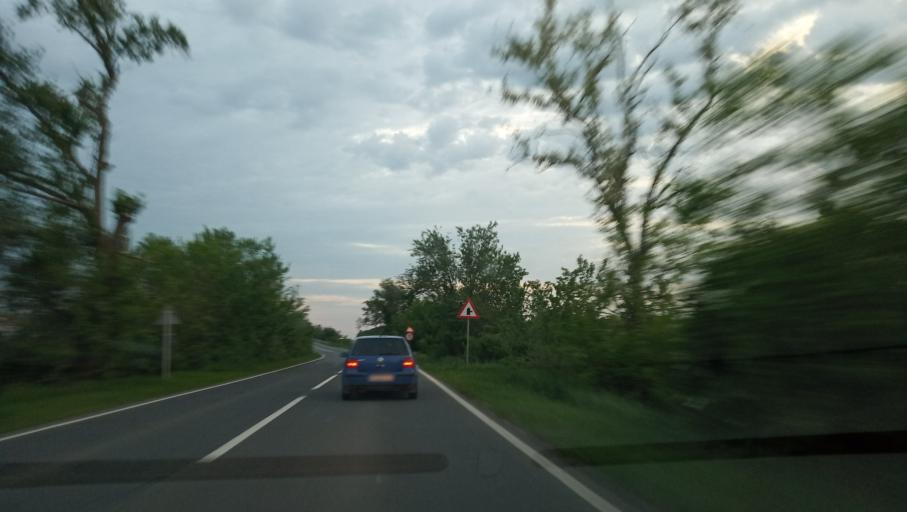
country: RO
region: Timis
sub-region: Comuna Sag
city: Sag
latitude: 45.6226
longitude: 21.1923
